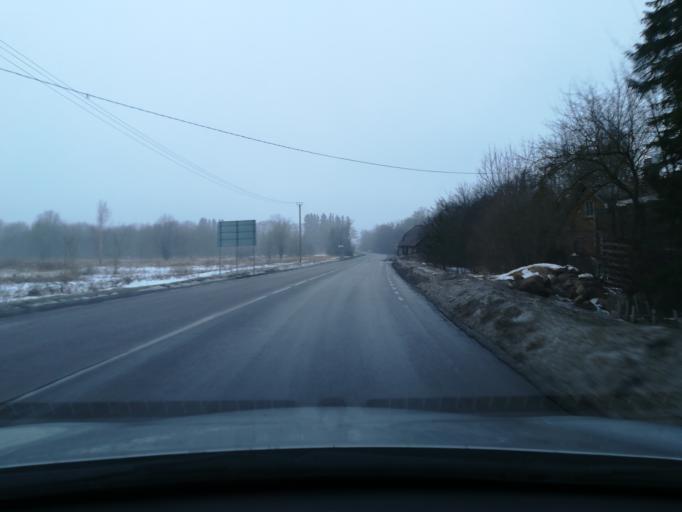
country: EE
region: Harju
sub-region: Rae vald
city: Jueri
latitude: 59.3603
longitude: 24.9236
